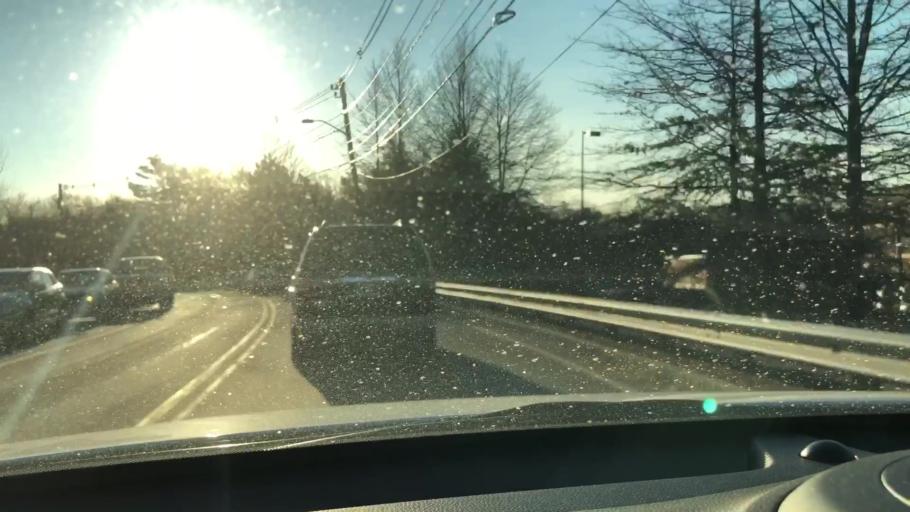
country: US
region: Massachusetts
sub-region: Plymouth County
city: Rockland
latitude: 42.1652
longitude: -70.8940
